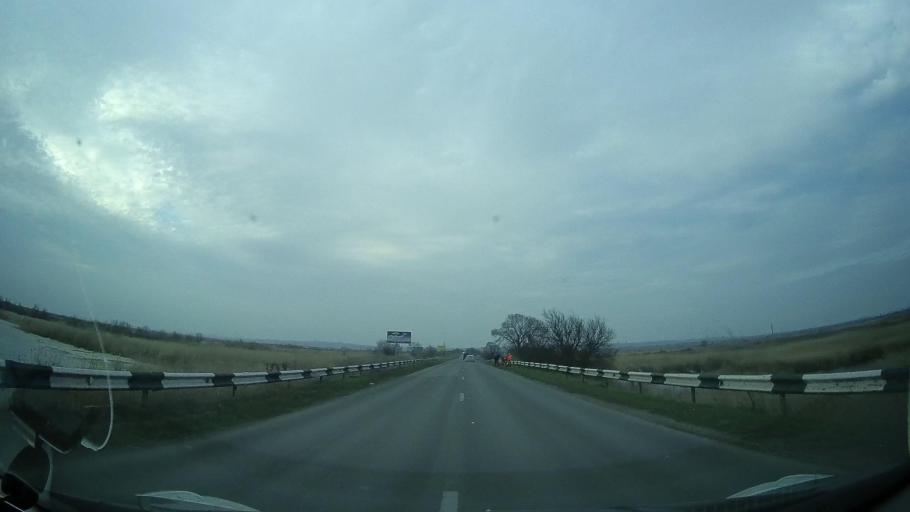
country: RU
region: Rostov
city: Ol'ginskaya
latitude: 47.2005
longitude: 39.9335
